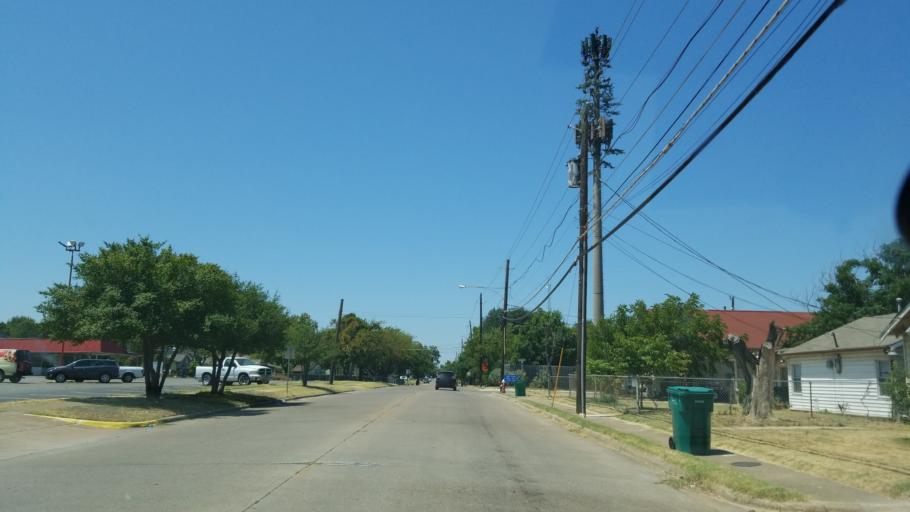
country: US
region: Texas
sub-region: Dallas County
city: Cockrell Hill
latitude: 32.7350
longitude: -96.8834
